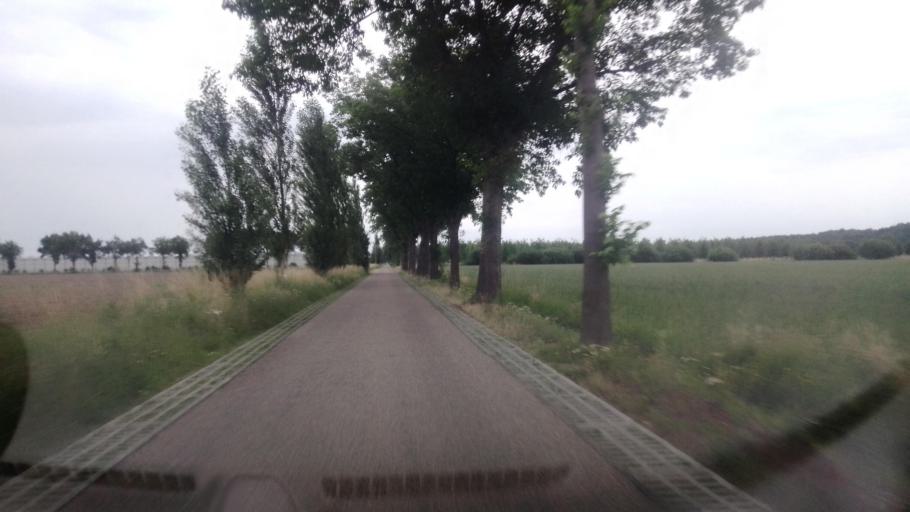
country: NL
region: Limburg
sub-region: Gemeente Beesel
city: Offenbeek
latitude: 51.2882
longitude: 6.1230
